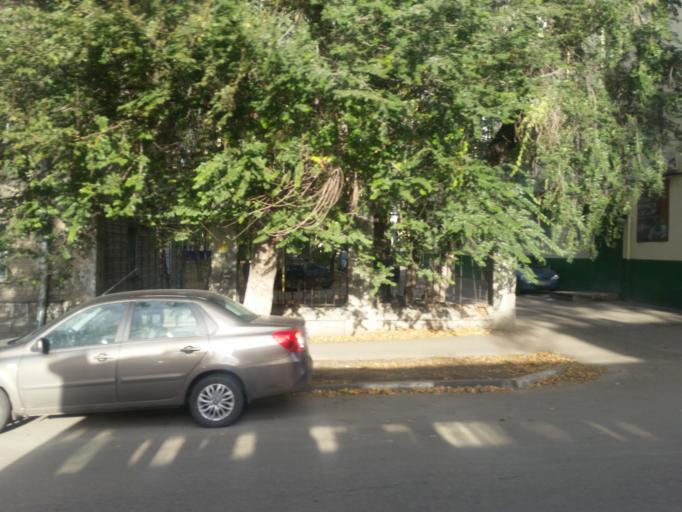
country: RU
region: Ulyanovsk
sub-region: Ulyanovskiy Rayon
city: Ulyanovsk
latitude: 54.3207
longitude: 48.3906
